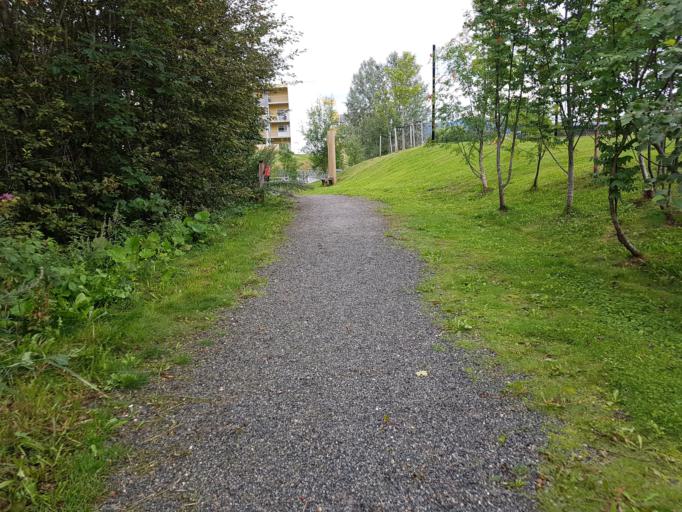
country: NO
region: Sor-Trondelag
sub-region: Trondheim
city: Trondheim
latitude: 63.3906
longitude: 10.4365
